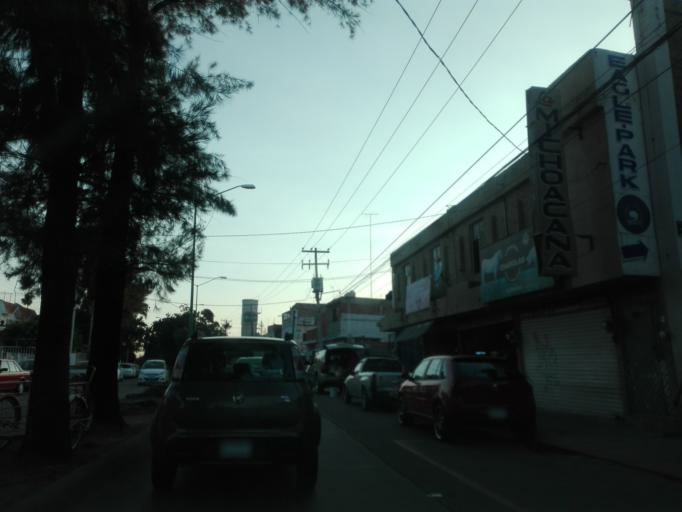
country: MX
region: Guanajuato
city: Leon
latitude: 21.1059
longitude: -101.6722
